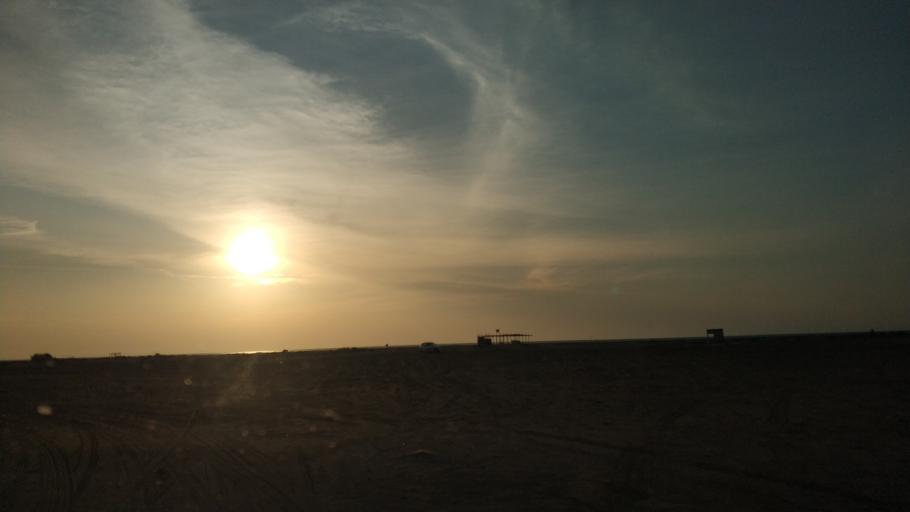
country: AL
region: Fier
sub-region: Rrethi i Lushnjes
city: Divjake
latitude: 40.9573
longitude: 19.4688
